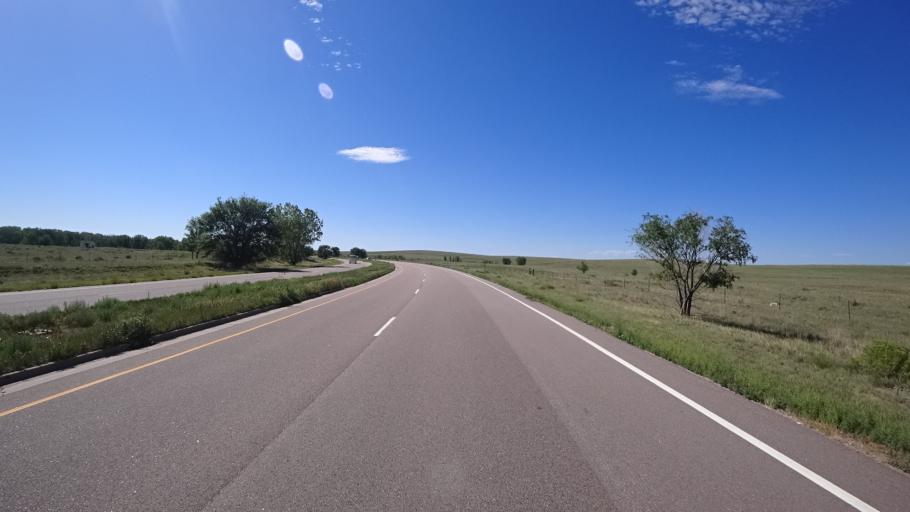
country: US
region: Colorado
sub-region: El Paso County
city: Security-Widefield
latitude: 38.7574
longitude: -104.6596
